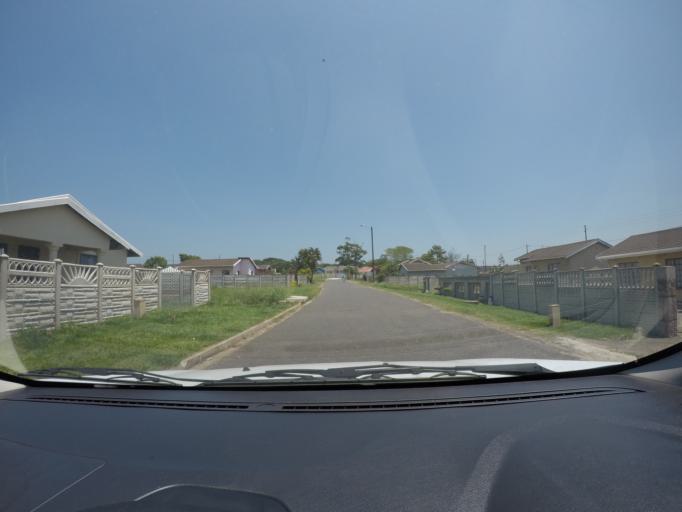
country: ZA
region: KwaZulu-Natal
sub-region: uThungulu District Municipality
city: eSikhawini
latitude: -28.8911
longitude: 31.8814
